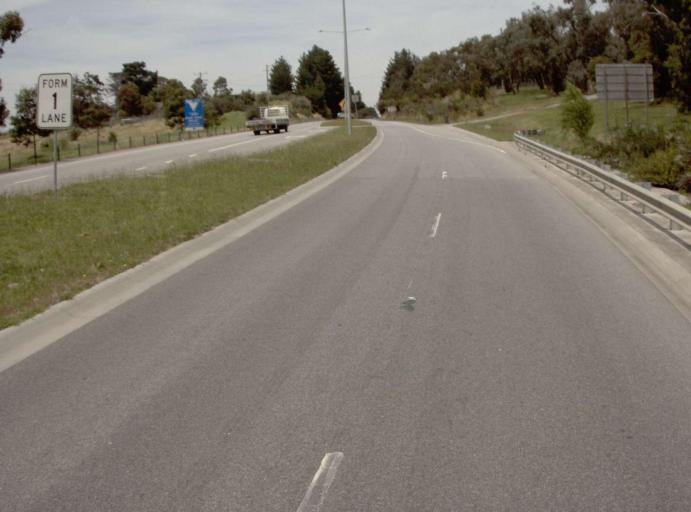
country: AU
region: Victoria
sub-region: Casey
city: Cranbourne South
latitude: -38.1695
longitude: 145.2215
